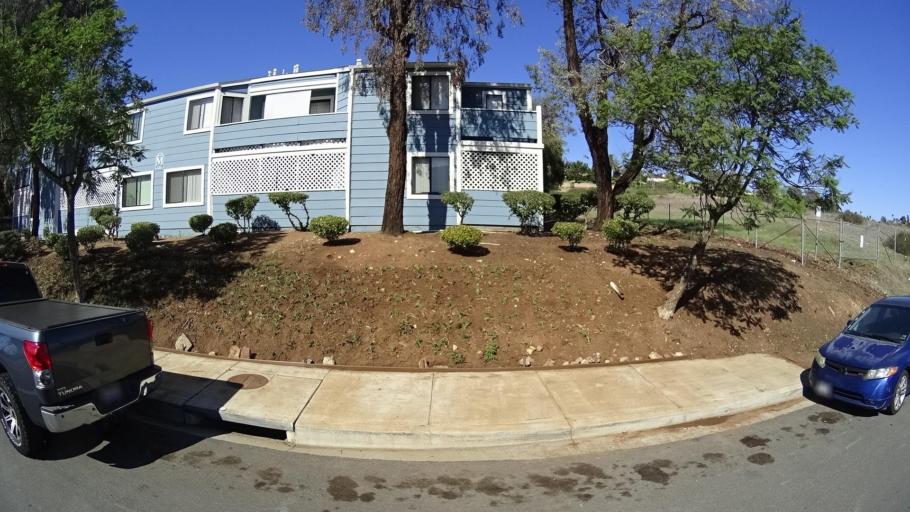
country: US
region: California
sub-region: San Diego County
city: Rancho San Diego
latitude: 32.7341
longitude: -116.9578
